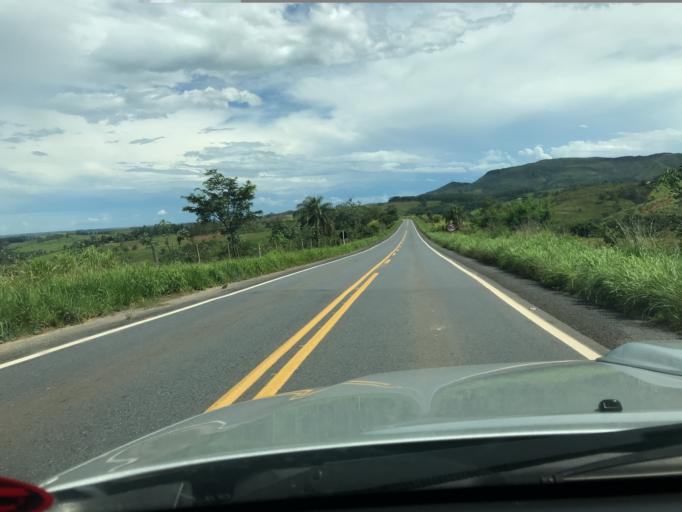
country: BR
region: Minas Gerais
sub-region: Campos Altos
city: Campos Altos
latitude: -19.7978
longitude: -46.0337
